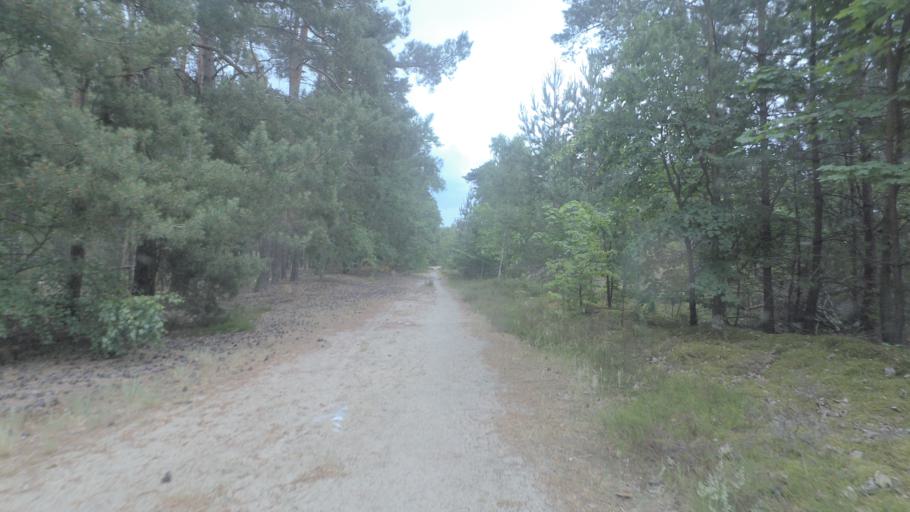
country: DE
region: Brandenburg
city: Ludwigsfelde
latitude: 52.3213
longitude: 13.2499
